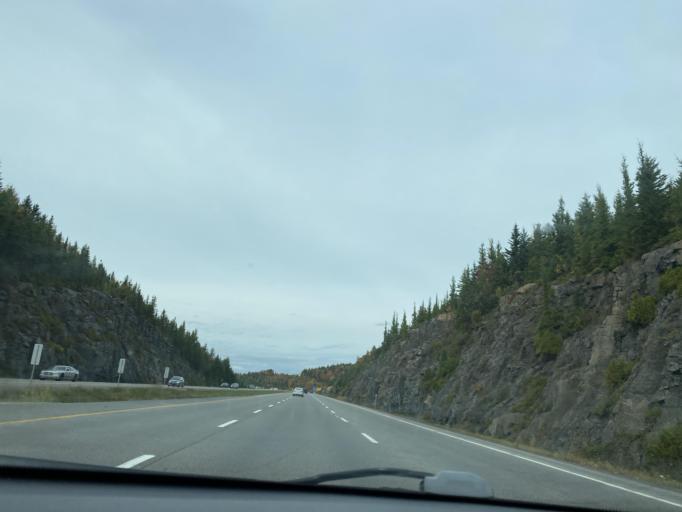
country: CA
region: Quebec
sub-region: Laurentides
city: Sainte-Adele
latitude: 45.9834
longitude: -74.1818
